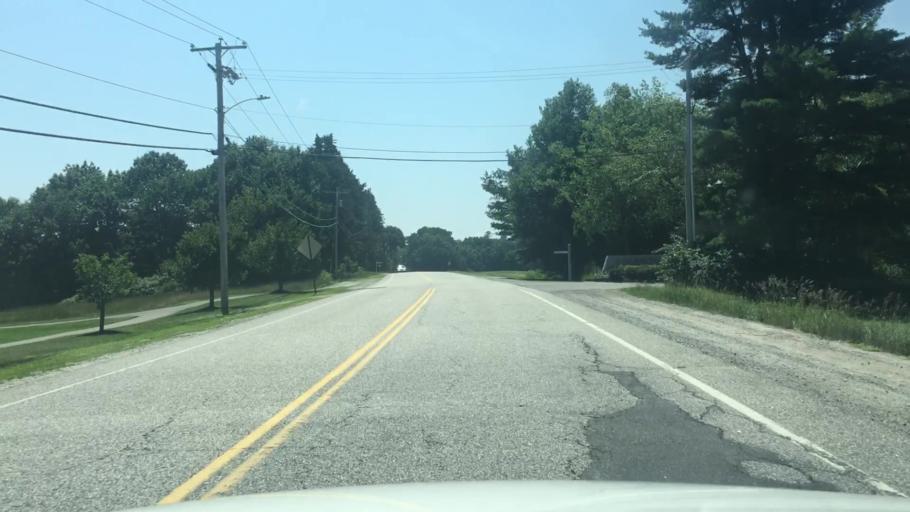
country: US
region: Maine
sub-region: Cumberland County
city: Cumberland Center
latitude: 43.7713
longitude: -70.2687
